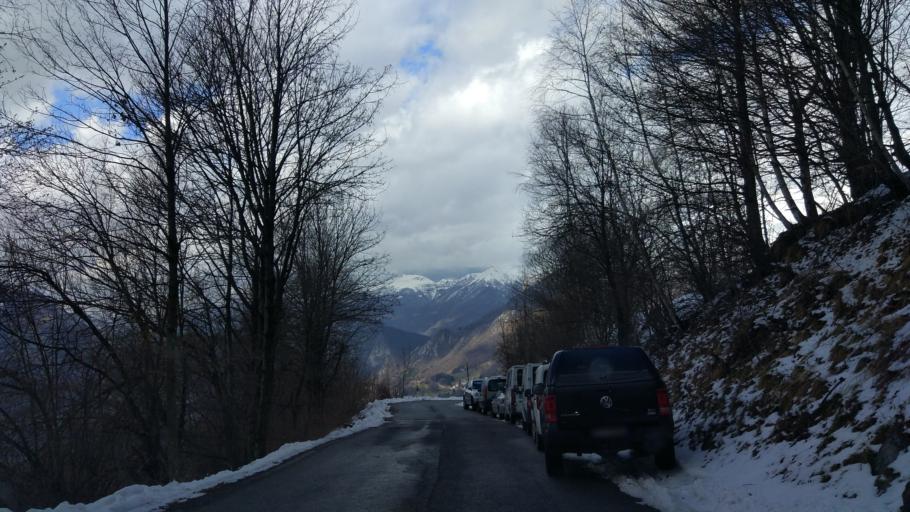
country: IT
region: Lombardy
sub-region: Provincia di Lecco
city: Moggio
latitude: 45.9102
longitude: 9.4967
